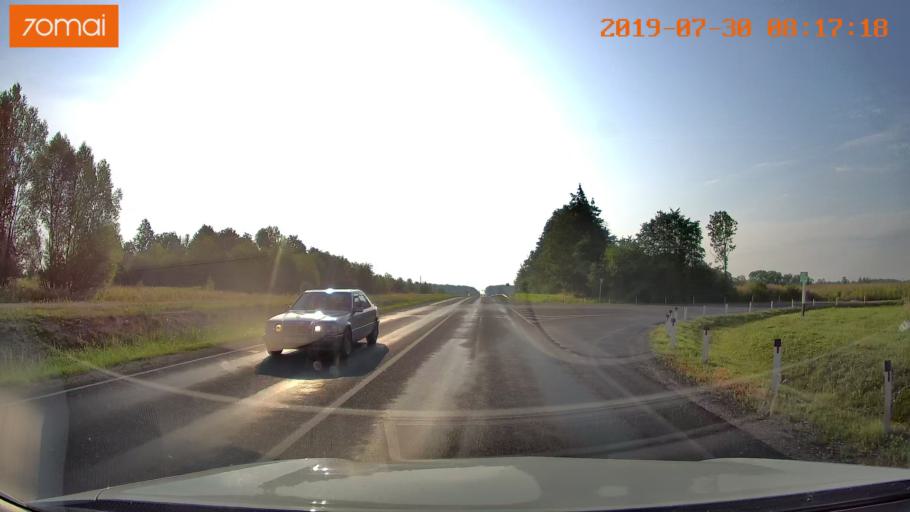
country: RU
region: Kaliningrad
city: Zheleznodorozhnyy
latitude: 54.6368
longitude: 21.4340
